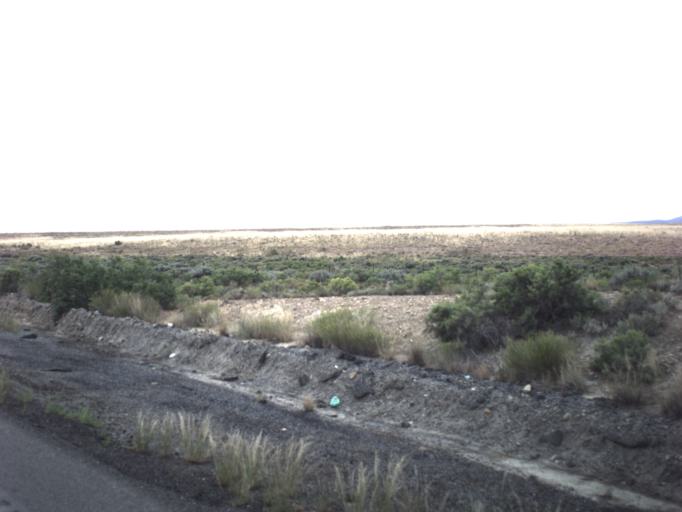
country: US
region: Utah
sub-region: Carbon County
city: East Carbon City
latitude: 39.5117
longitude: -110.5408
